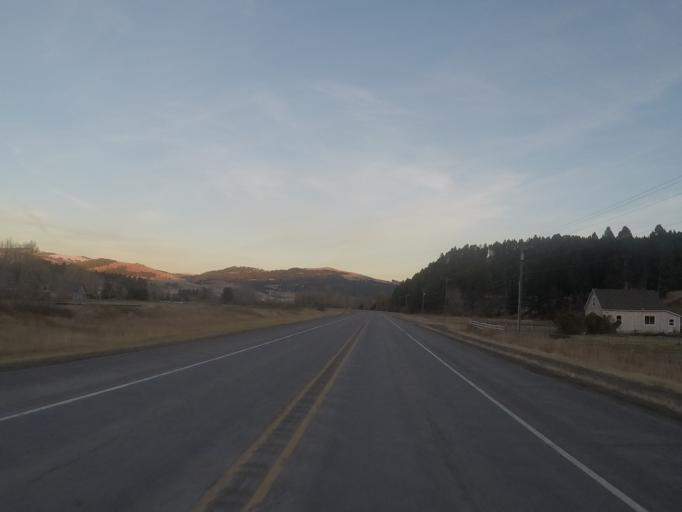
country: US
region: Montana
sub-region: Lewis and Clark County
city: Helena West Side
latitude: 46.5586
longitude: -112.4229
